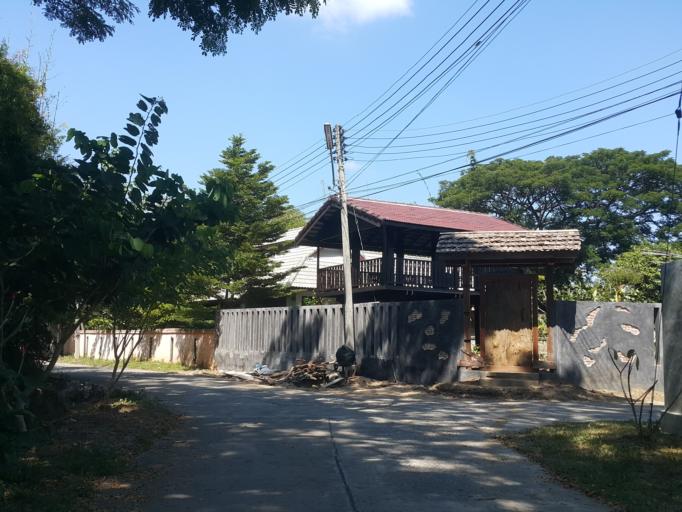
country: TH
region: Chiang Mai
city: Saraphi
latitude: 18.7647
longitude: 99.0505
